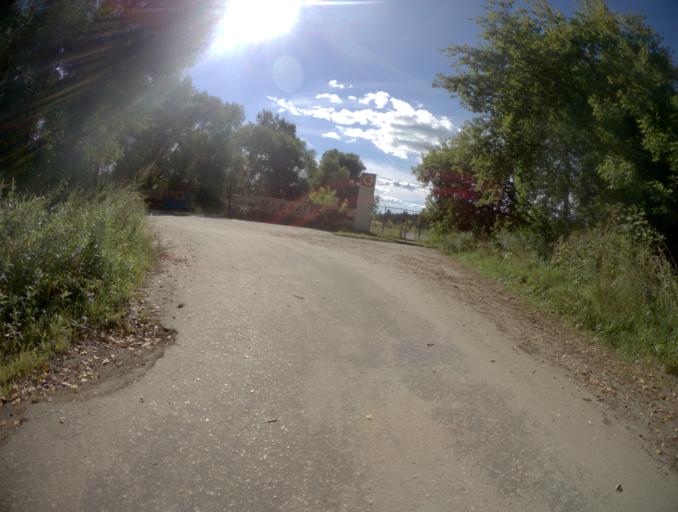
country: RU
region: Vladimir
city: Krasnaya Gorbatka
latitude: 55.8647
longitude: 41.7534
